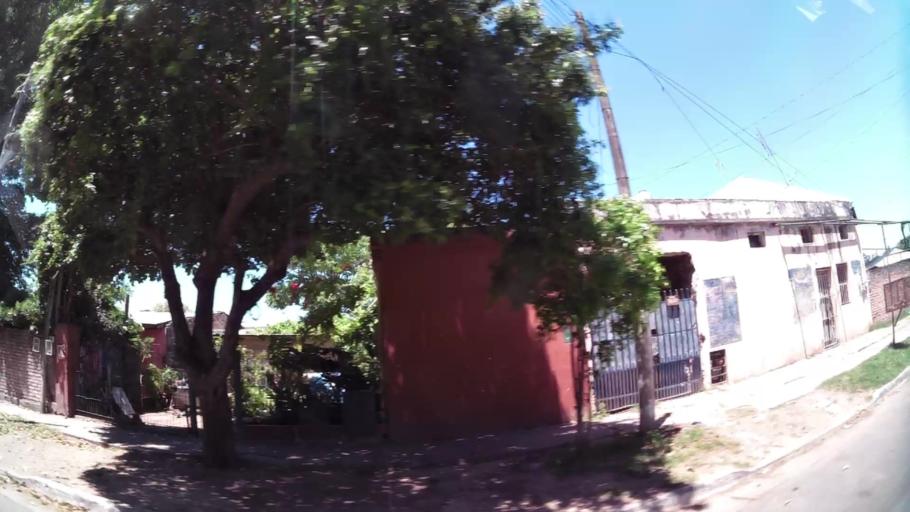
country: AR
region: Buenos Aires
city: Hurlingham
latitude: -34.5081
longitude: -58.7093
